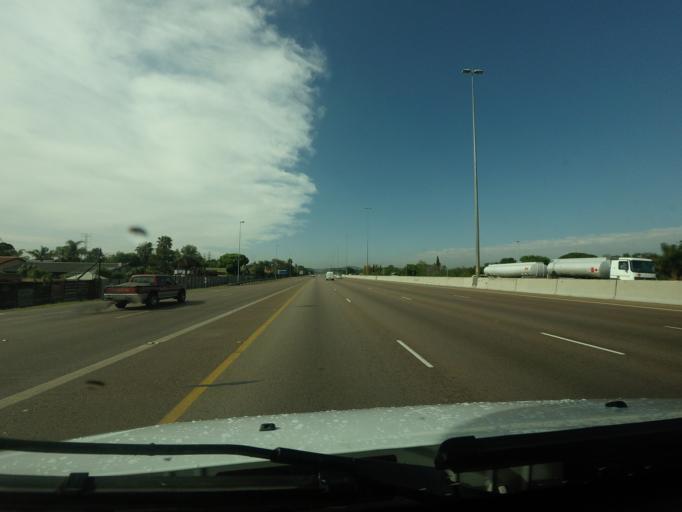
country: ZA
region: Gauteng
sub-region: City of Tshwane Metropolitan Municipality
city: Pretoria
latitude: -25.7148
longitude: 28.2657
